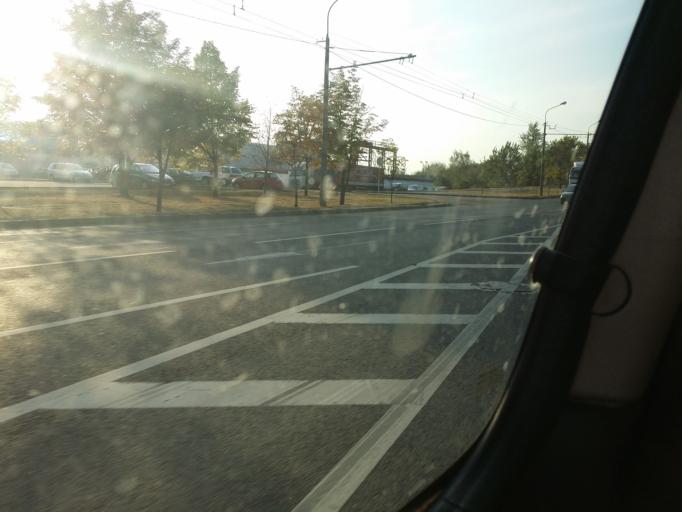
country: BY
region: Minsk
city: Minsk
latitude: 53.8998
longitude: 27.6391
